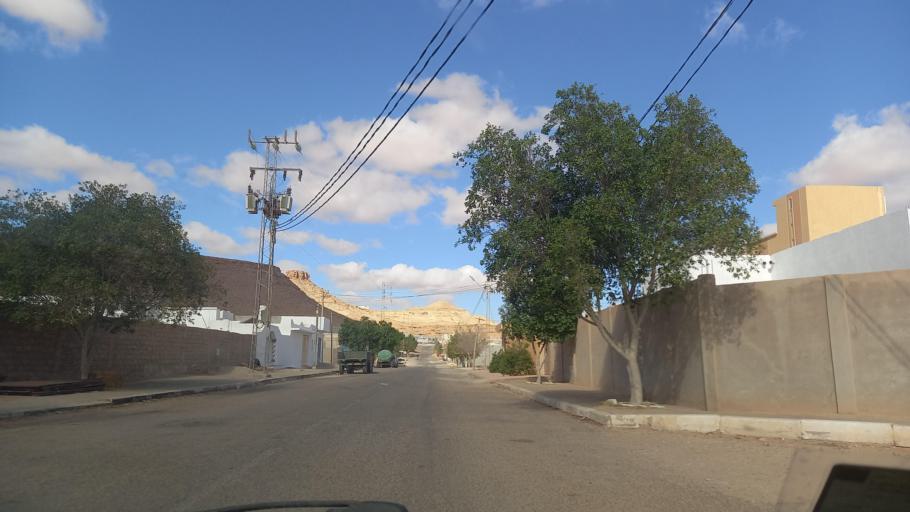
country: TN
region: Tataouine
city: Tataouine
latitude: 32.9809
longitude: 10.2673
